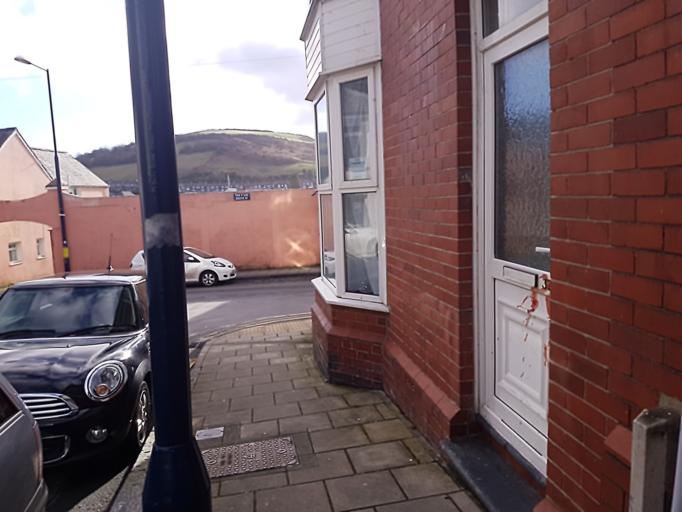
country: GB
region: Wales
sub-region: County of Ceredigion
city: Aberystwyth
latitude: 52.4122
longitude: -4.0862
